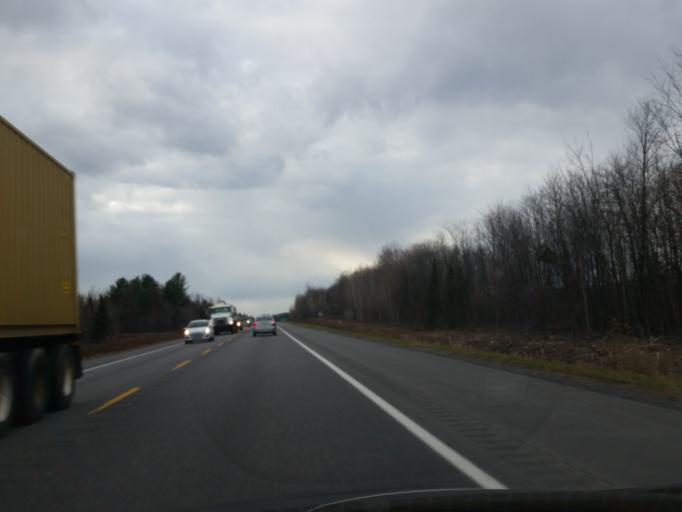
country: CA
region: Quebec
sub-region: Laurentides
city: Saint-Colomban
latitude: 45.6816
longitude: -74.1427
